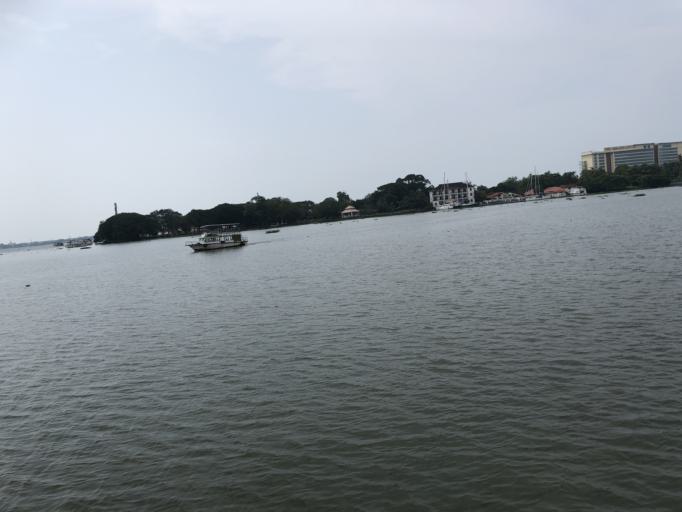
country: IN
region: Kerala
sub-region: Ernakulam
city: Cochin
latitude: 9.9853
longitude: 76.2715
